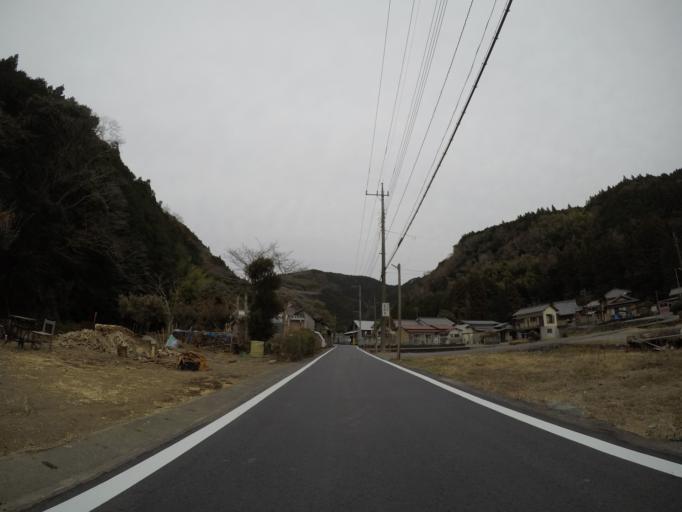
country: JP
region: Shizuoka
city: Fujinomiya
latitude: 35.2330
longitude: 138.5347
